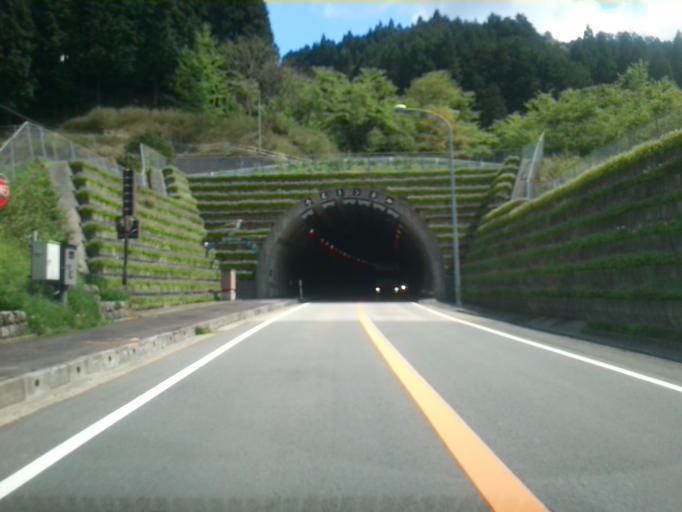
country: JP
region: Kyoto
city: Fukuchiyama
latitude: 35.4165
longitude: 135.0387
